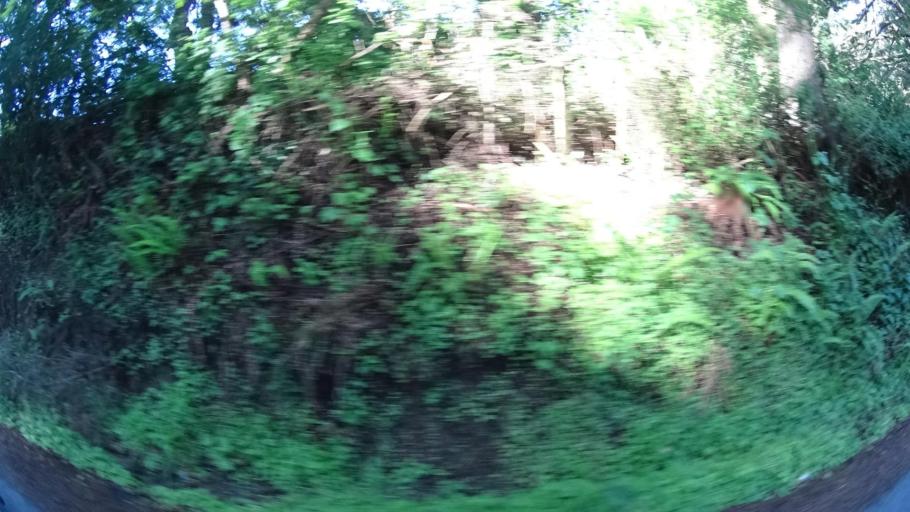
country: US
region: California
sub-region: Humboldt County
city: McKinleyville
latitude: 40.9810
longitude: -124.0974
